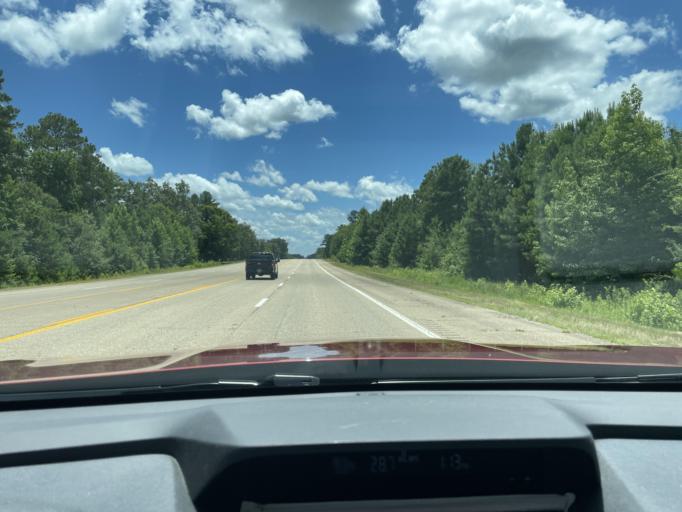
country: US
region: Arkansas
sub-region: Drew County
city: Monticello
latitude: 33.6827
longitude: -91.8054
